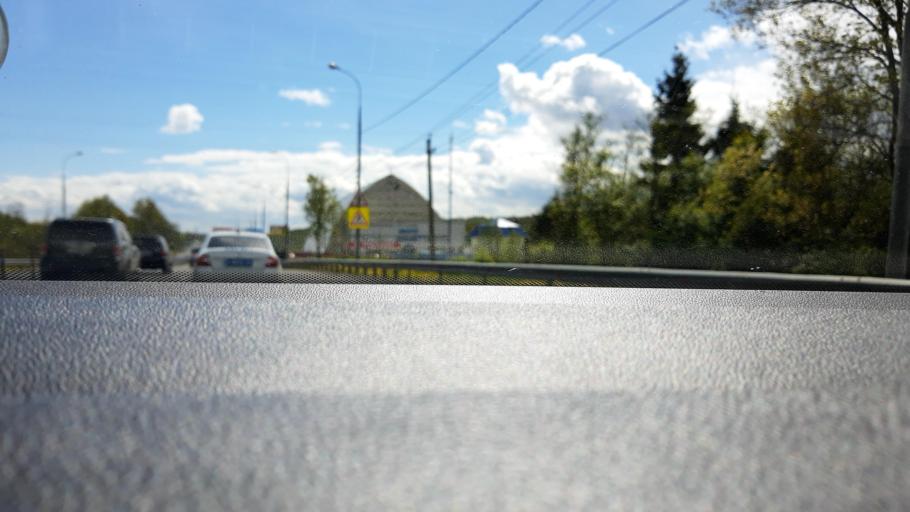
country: RU
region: Moskovskaya
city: Podosinki
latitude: 56.2114
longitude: 37.5218
